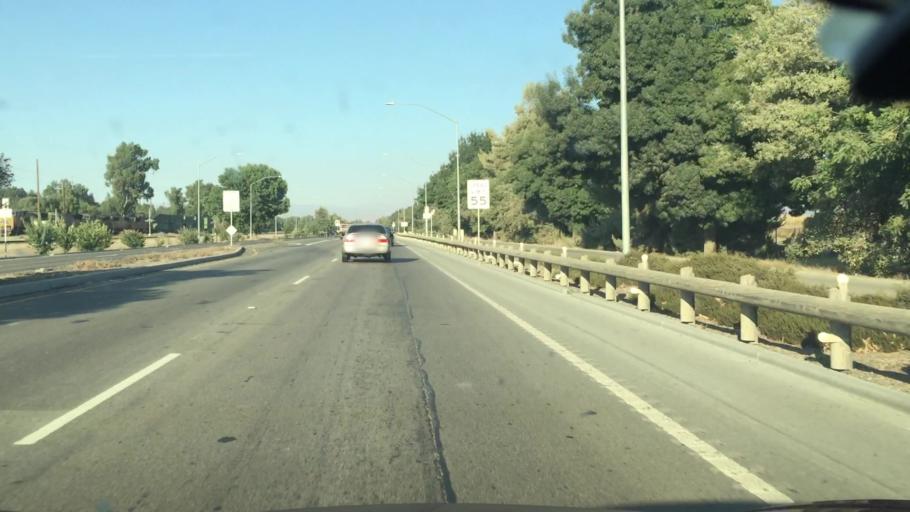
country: US
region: California
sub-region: Alameda County
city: Pleasanton
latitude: 37.6735
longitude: -121.8287
